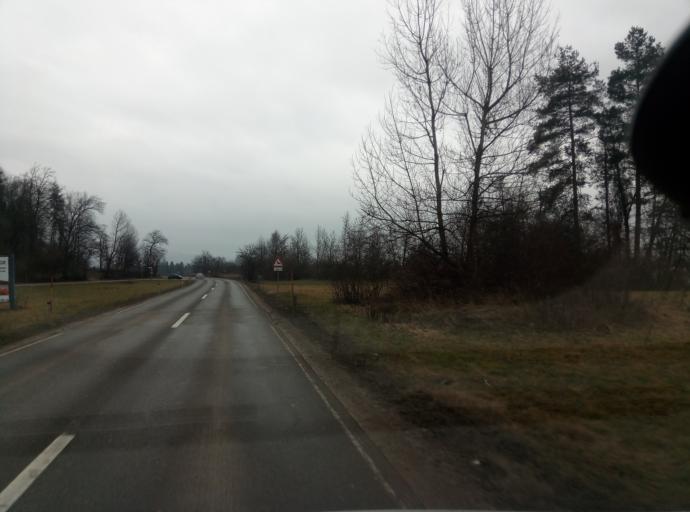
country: SI
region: Trzin
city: Trzin
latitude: 46.0948
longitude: 14.5609
